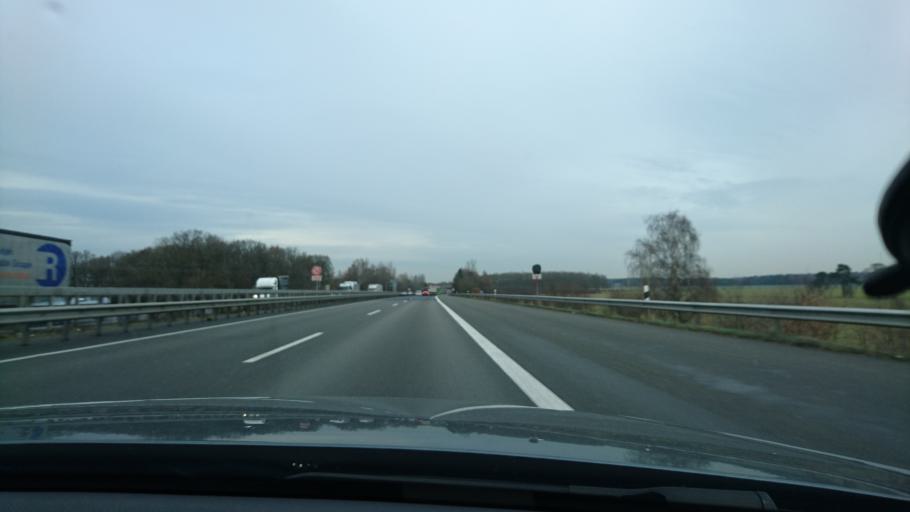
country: DE
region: Lower Saxony
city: Wallenhorst
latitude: 52.4062
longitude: 8.0334
